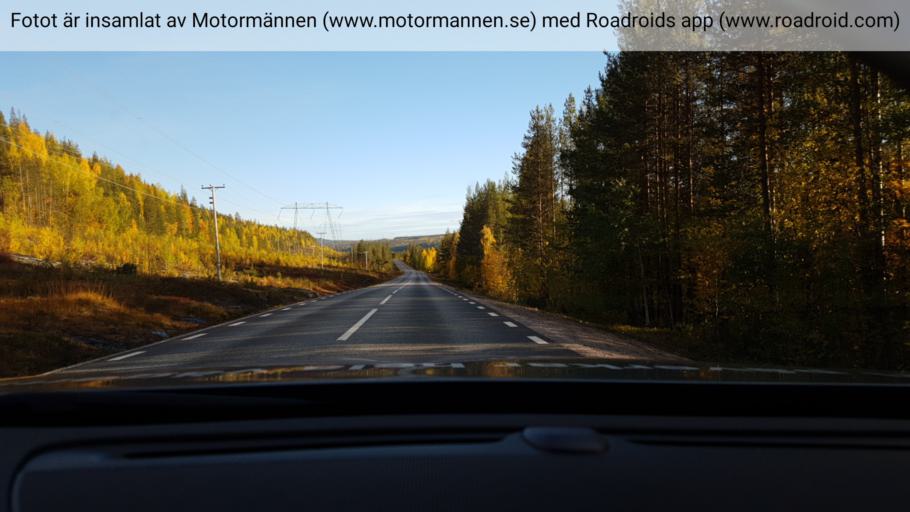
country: SE
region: Norrbotten
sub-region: Jokkmokks Kommun
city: Jokkmokk
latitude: 66.8456
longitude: 19.8360
